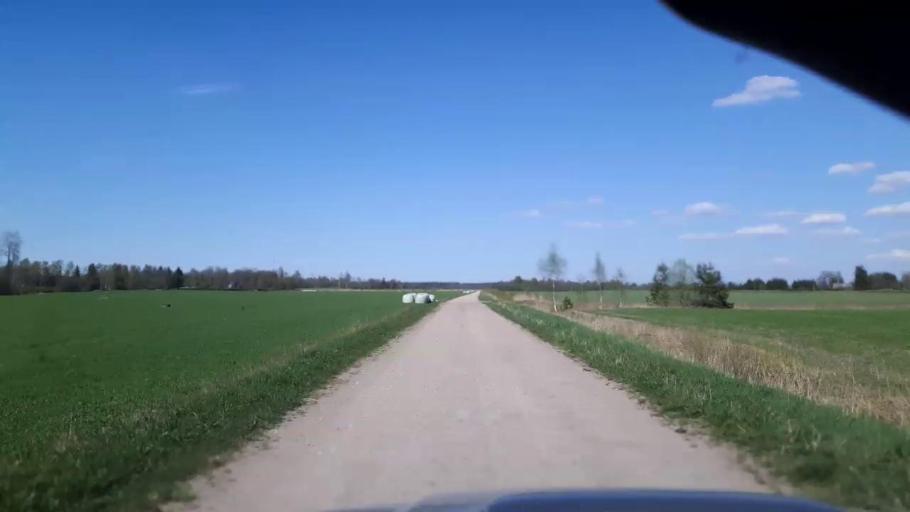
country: EE
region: Paernumaa
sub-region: Tootsi vald
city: Tootsi
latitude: 58.5266
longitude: 24.8232
